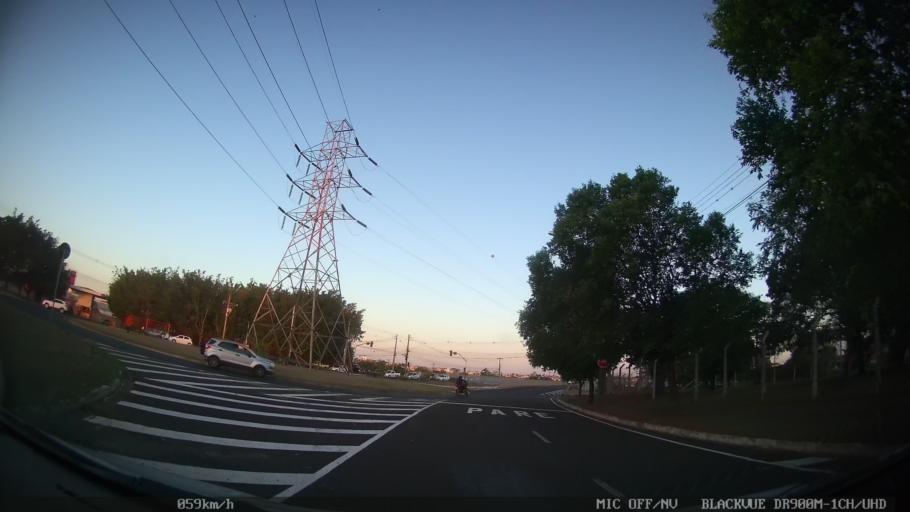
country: BR
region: Sao Paulo
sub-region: Sao Jose Do Rio Preto
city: Sao Jose do Rio Preto
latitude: -20.8007
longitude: -49.3461
